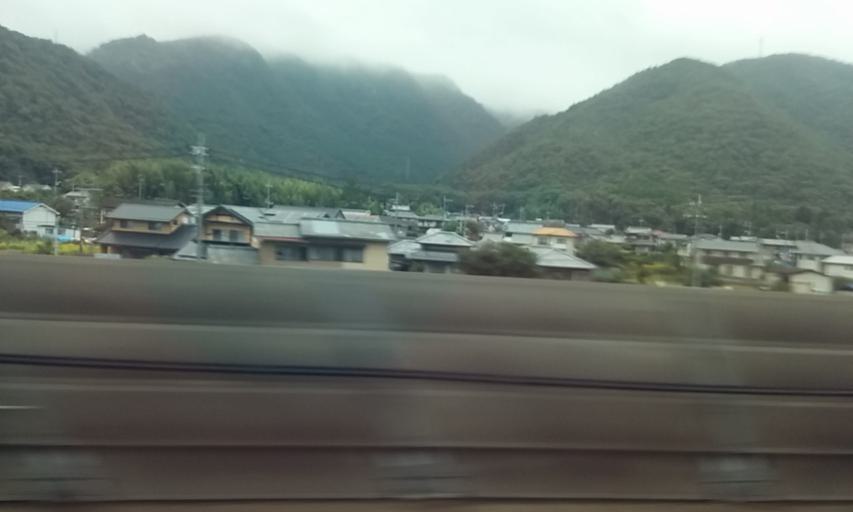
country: JP
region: Okayama
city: Okayama-shi
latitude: 34.7336
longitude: 134.1357
